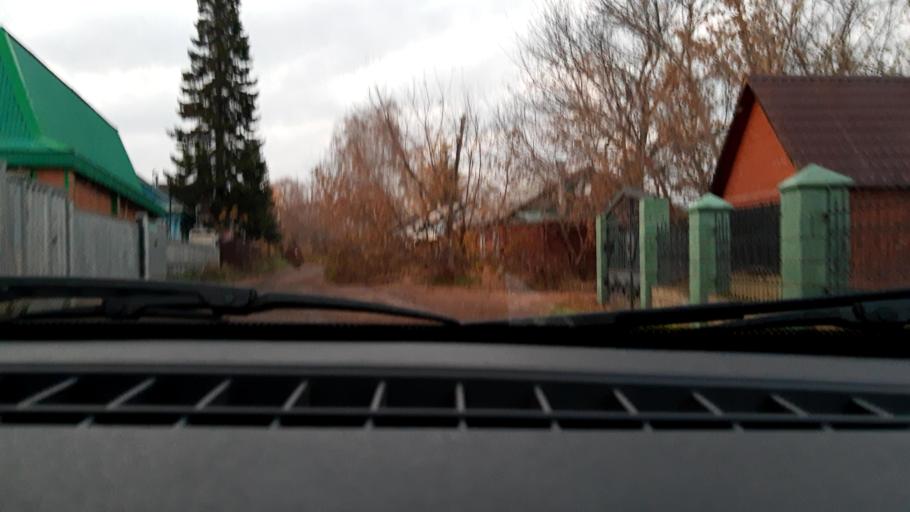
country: RU
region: Bashkortostan
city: Mikhaylovka
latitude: 54.7828
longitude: 55.8839
